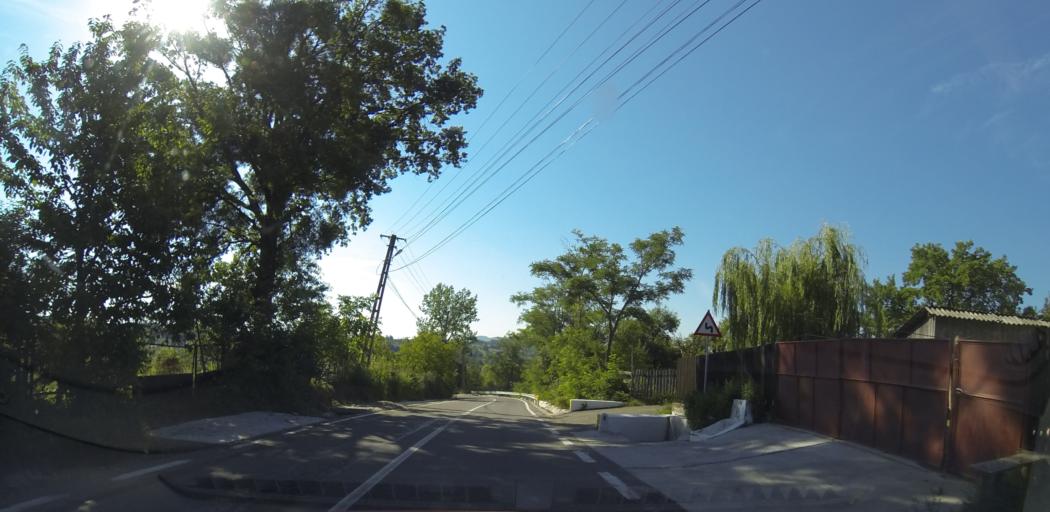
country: RO
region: Valcea
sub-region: Comuna Vaideeni
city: Vaideeni
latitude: 45.1705
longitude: 23.8753
